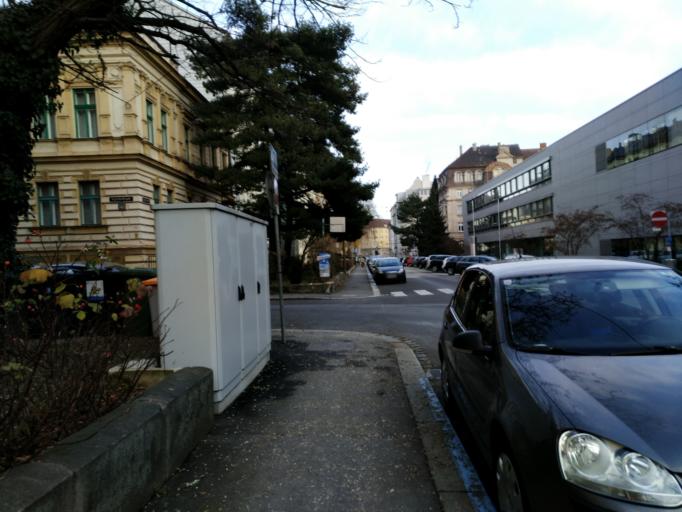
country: AT
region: Upper Austria
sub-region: Linz Stadt
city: Linz
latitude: 48.2935
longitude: 14.2880
